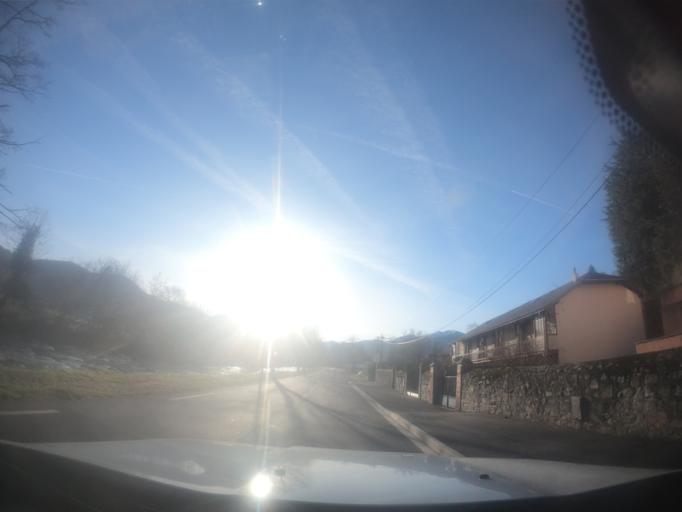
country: FR
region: Midi-Pyrenees
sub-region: Departement des Hautes-Pyrenees
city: Gerde
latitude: 43.0568
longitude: 0.1561
